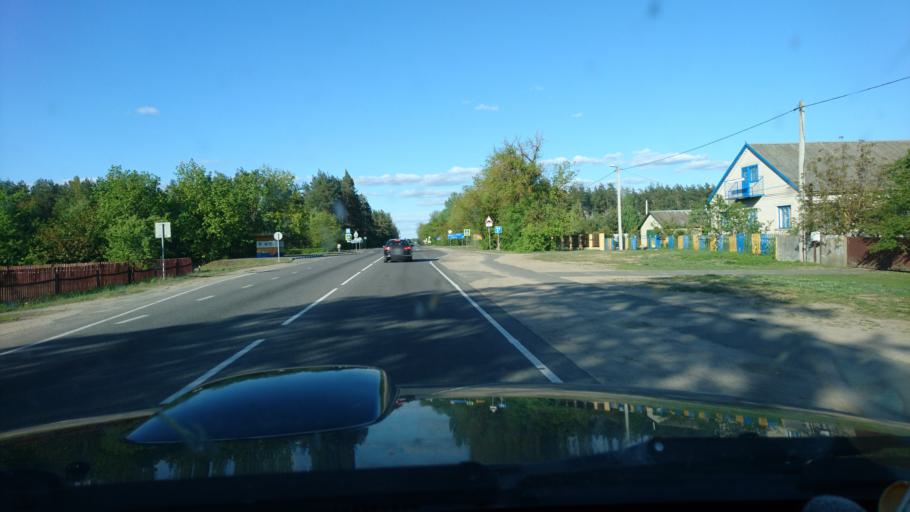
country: BY
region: Brest
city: Byaroza
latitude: 52.5456
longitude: 25.0074
